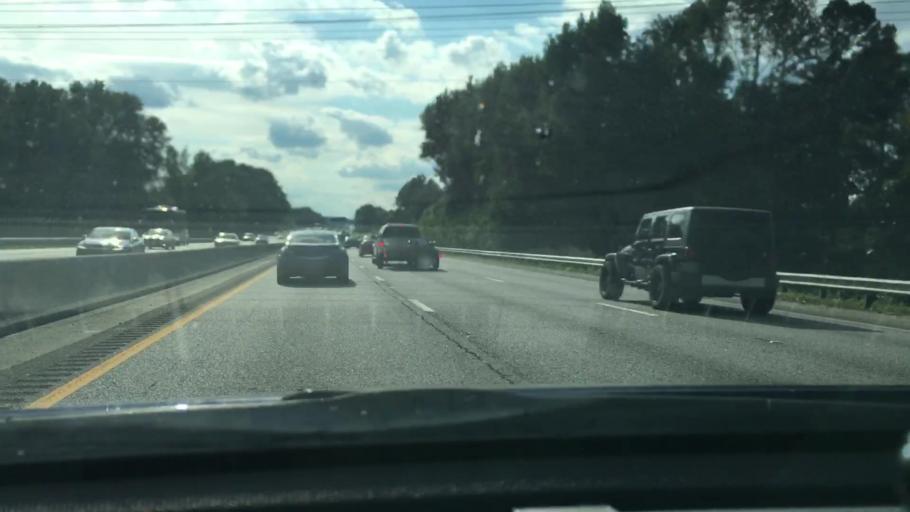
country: US
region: South Carolina
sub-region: Richland County
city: Columbia
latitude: 34.0532
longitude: -81.0613
